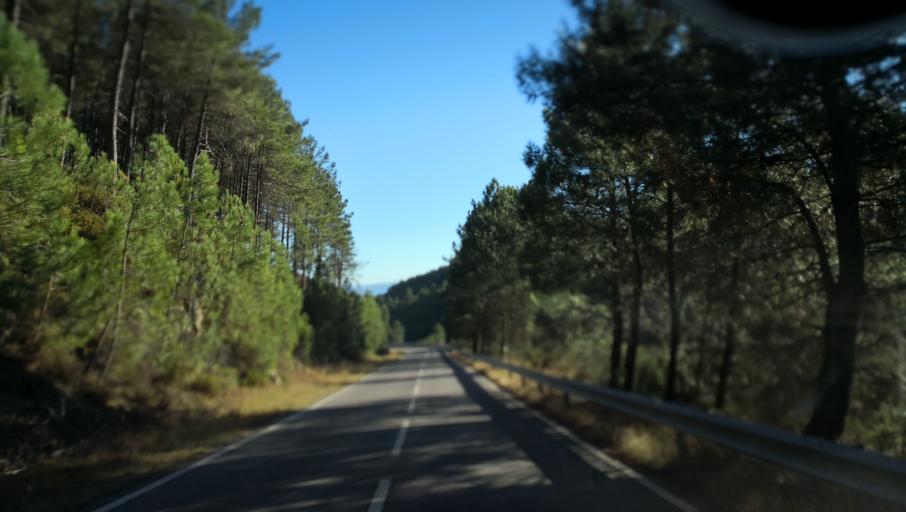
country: PT
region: Vila Real
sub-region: Vila Real
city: Vila Real
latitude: 41.3370
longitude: -7.7786
